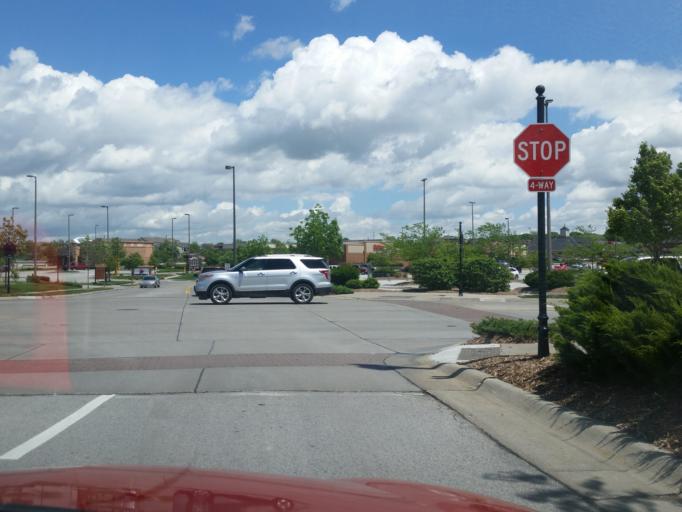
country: US
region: Nebraska
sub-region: Sarpy County
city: Papillion
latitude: 41.1367
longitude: -96.0297
